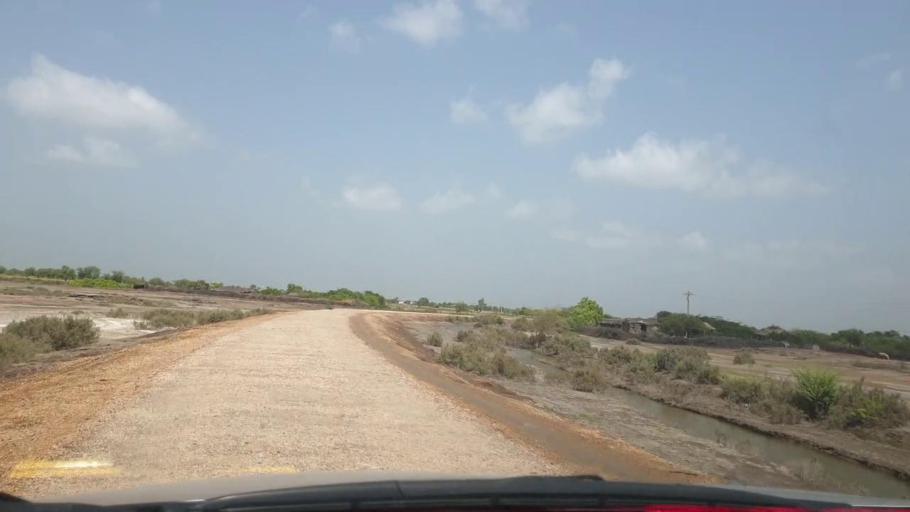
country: PK
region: Sindh
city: Rajo Khanani
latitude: 24.9236
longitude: 68.8978
